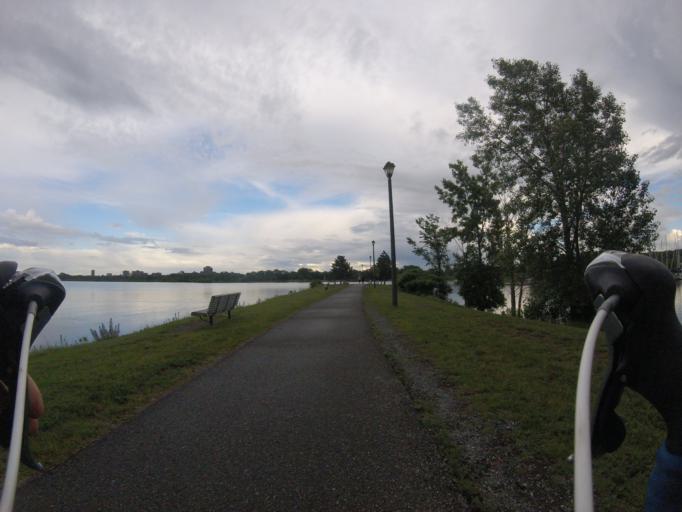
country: CA
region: Ontario
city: Bells Corners
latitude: 45.3539
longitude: -75.8254
